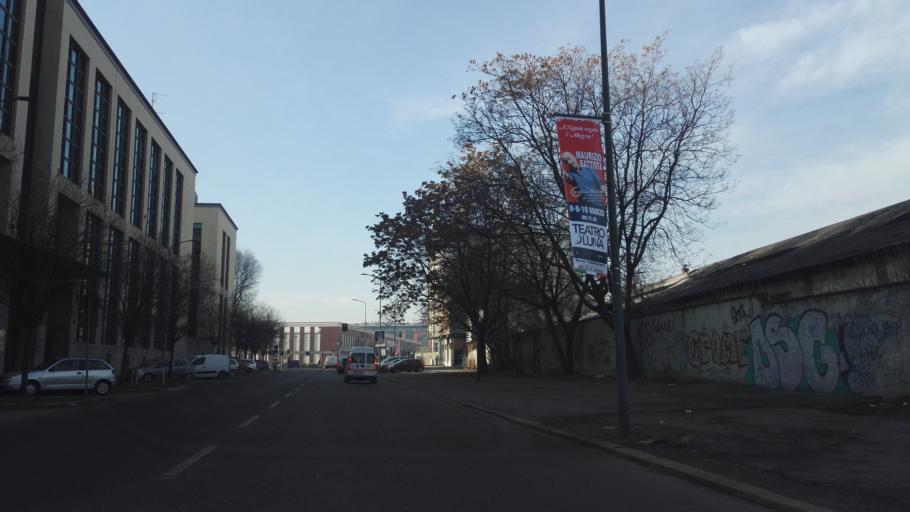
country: IT
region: Lombardy
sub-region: Citta metropolitana di Milano
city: Milano
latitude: 45.4437
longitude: 9.2006
